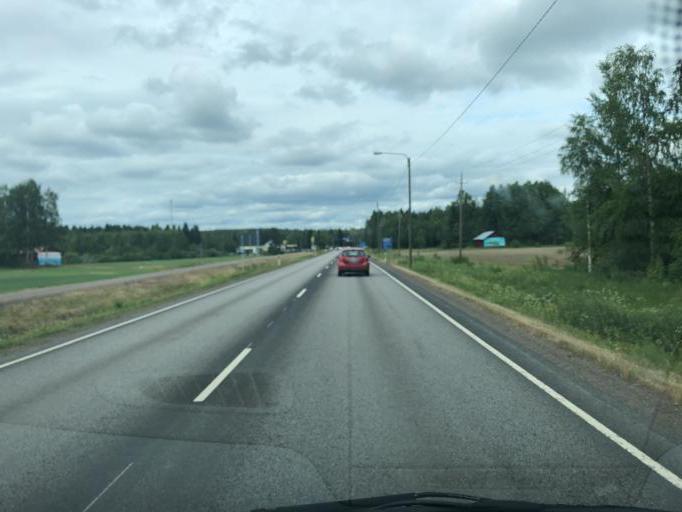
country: FI
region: Kymenlaakso
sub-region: Kouvola
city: Kouvola
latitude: 60.9255
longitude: 26.7949
